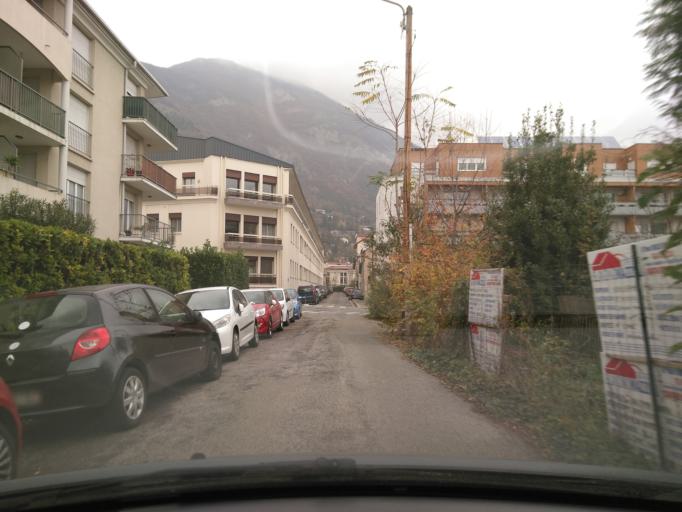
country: FR
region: Rhone-Alpes
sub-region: Departement de l'Isere
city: La Tronche
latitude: 45.2002
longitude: 5.7372
